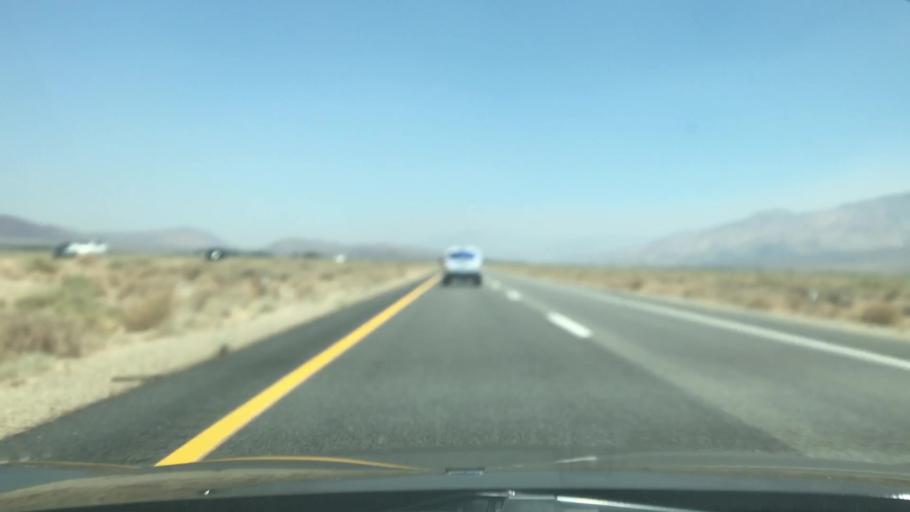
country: US
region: California
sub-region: Inyo County
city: Big Pine
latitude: 36.9514
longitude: -118.2402
